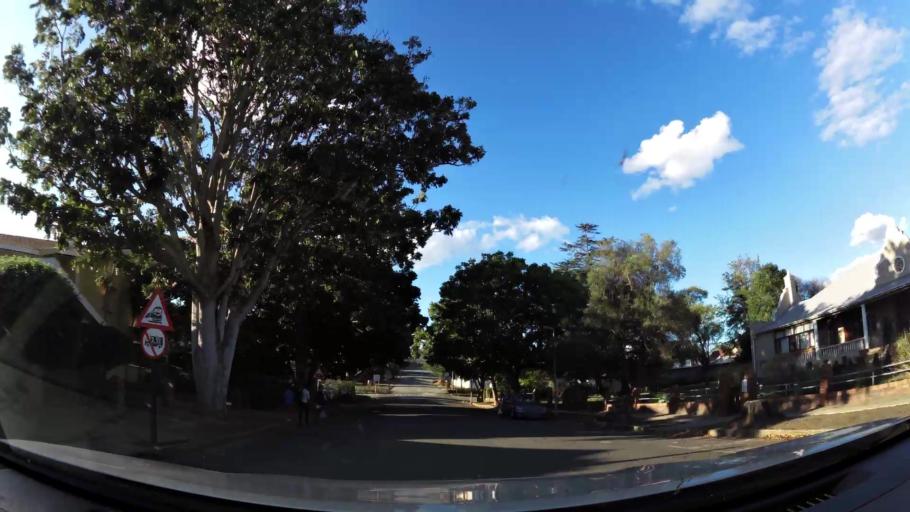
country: ZA
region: Western Cape
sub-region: Eden District Municipality
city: Riversdale
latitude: -34.0888
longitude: 20.9579
